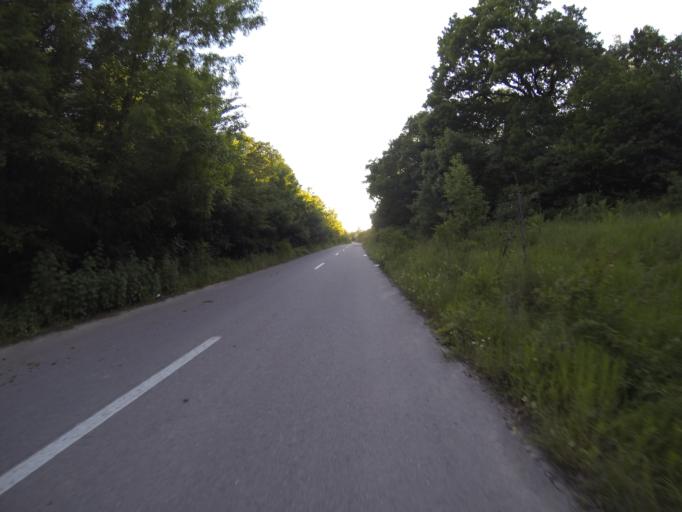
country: RO
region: Dolj
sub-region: Comuna Tuglui
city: Tuglui
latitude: 44.1620
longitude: 23.8055
